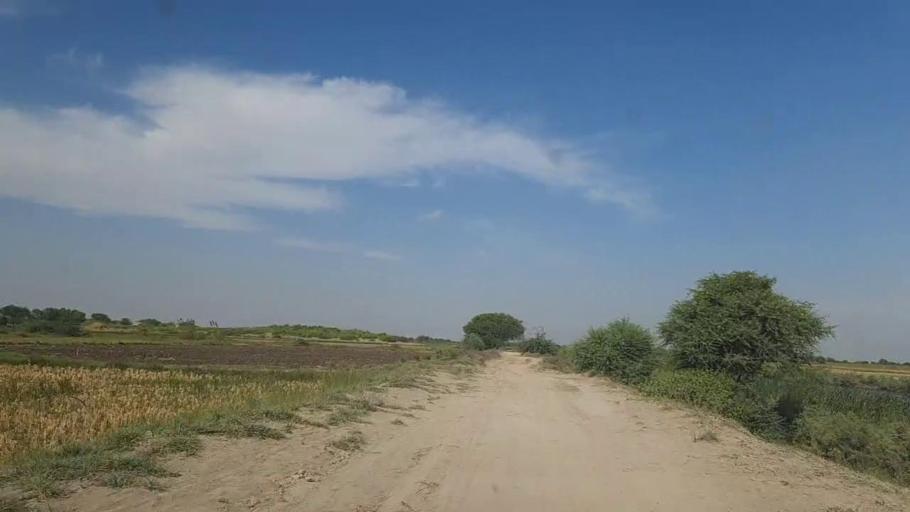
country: PK
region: Sindh
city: Bulri
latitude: 24.8162
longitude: 68.2661
